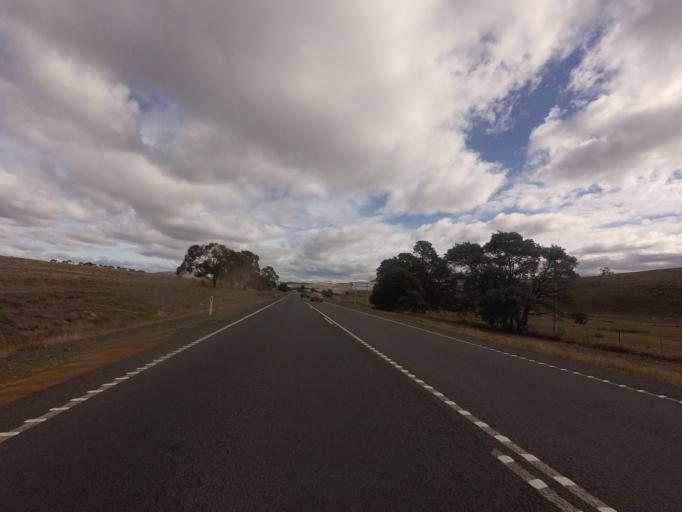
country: AU
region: Tasmania
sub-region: Brighton
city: Bridgewater
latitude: -42.4614
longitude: 147.1909
